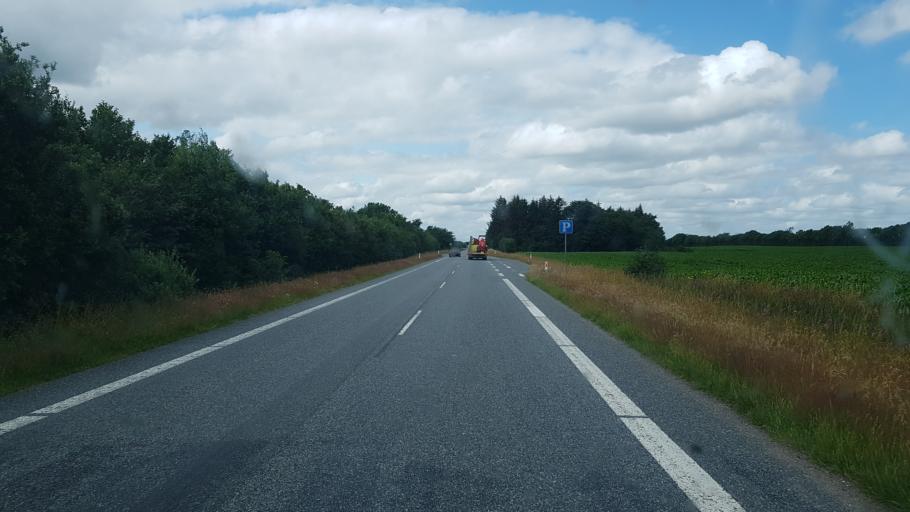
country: DK
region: South Denmark
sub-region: Vejen Kommune
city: Holsted
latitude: 55.5181
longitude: 8.8327
